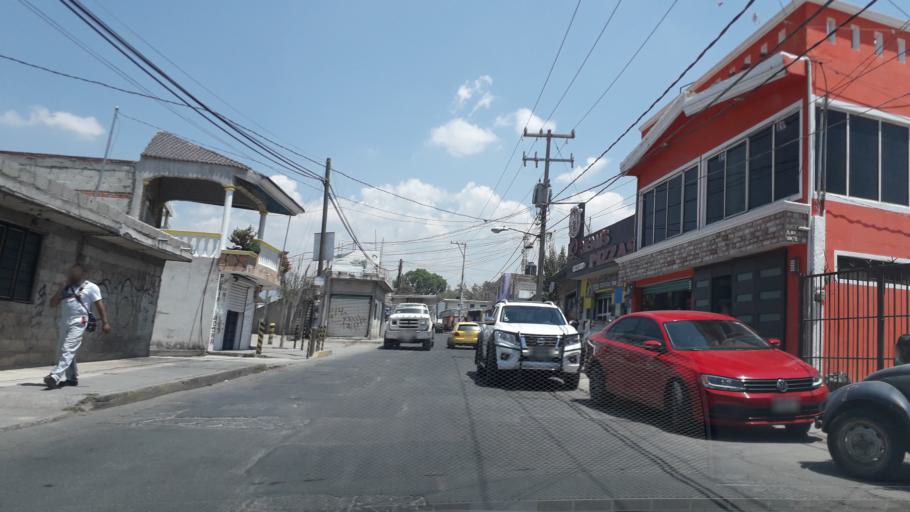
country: MX
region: Puebla
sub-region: Puebla
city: Santa Maria Xonacatepec
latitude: 19.0812
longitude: -98.1086
